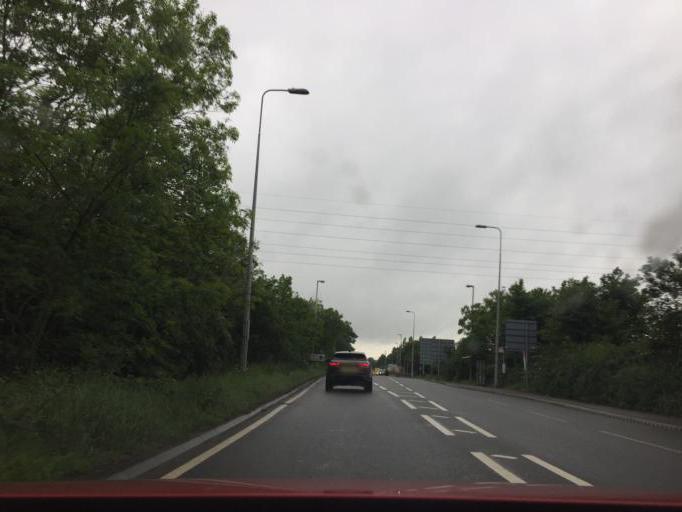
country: GB
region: England
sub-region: Leicestershire
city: Stoke Golding
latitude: 52.5347
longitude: -1.4142
